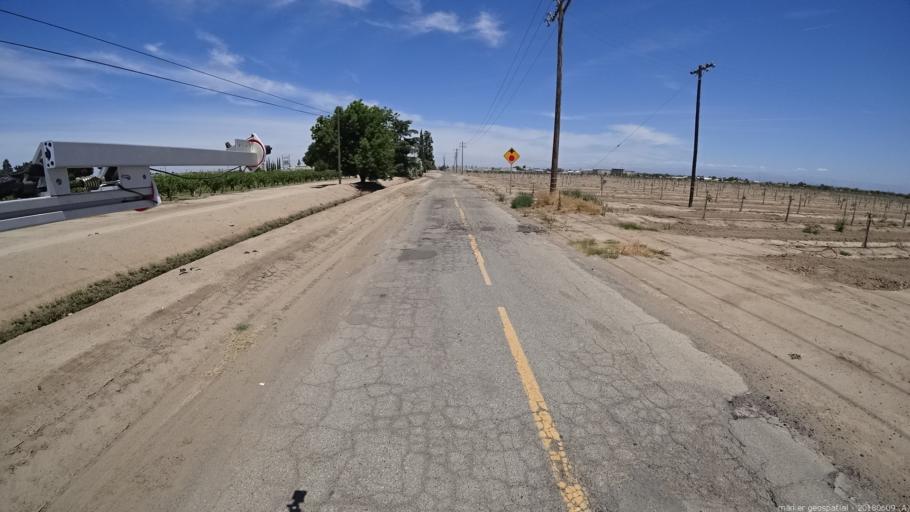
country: US
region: California
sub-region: Madera County
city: Madera
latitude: 36.9364
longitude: -120.0831
